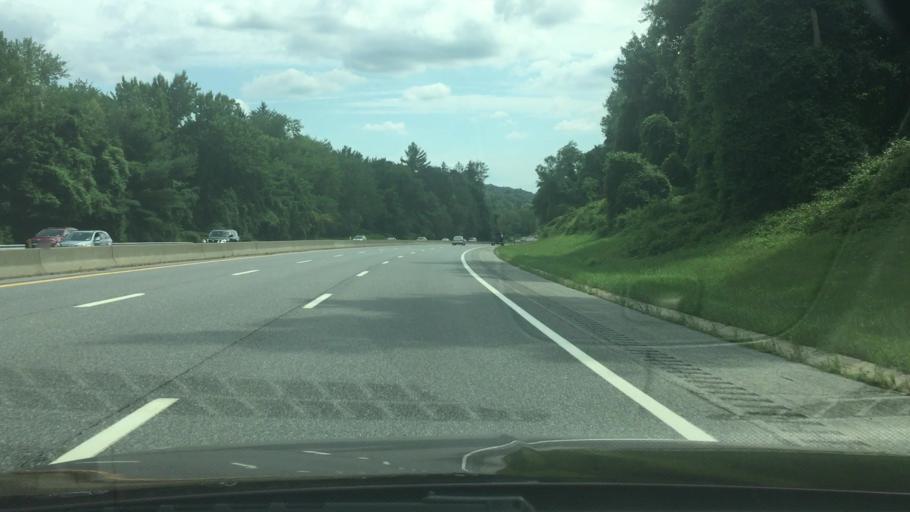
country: US
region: New York
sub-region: Westchester County
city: Briarcliff Manor
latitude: 41.1542
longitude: -73.8169
